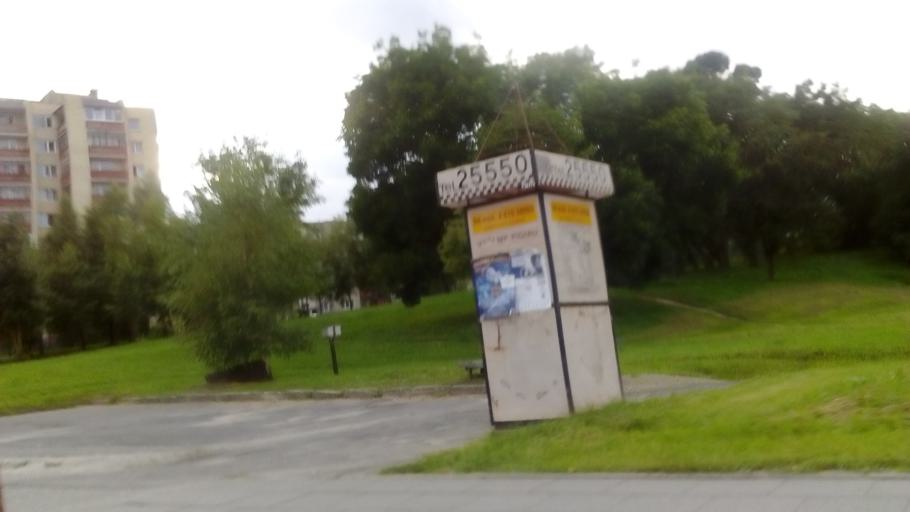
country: LT
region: Alytaus apskritis
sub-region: Alytus
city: Alytus
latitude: 54.3971
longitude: 24.0276
